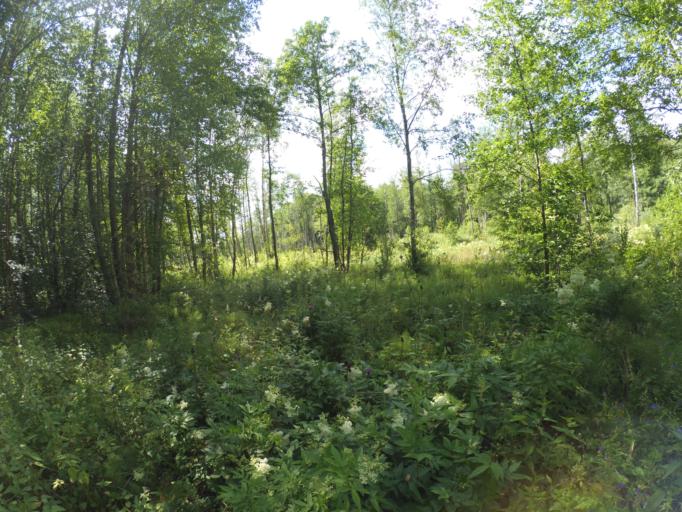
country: RU
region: Moskovskaya
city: Fosforitnyy
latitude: 55.3387
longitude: 38.9378
